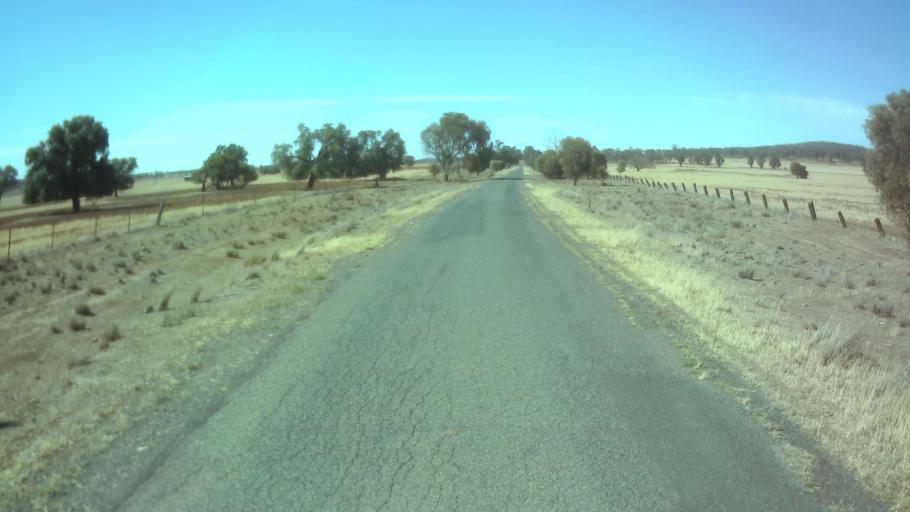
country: AU
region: New South Wales
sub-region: Forbes
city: Forbes
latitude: -33.7419
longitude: 147.7405
